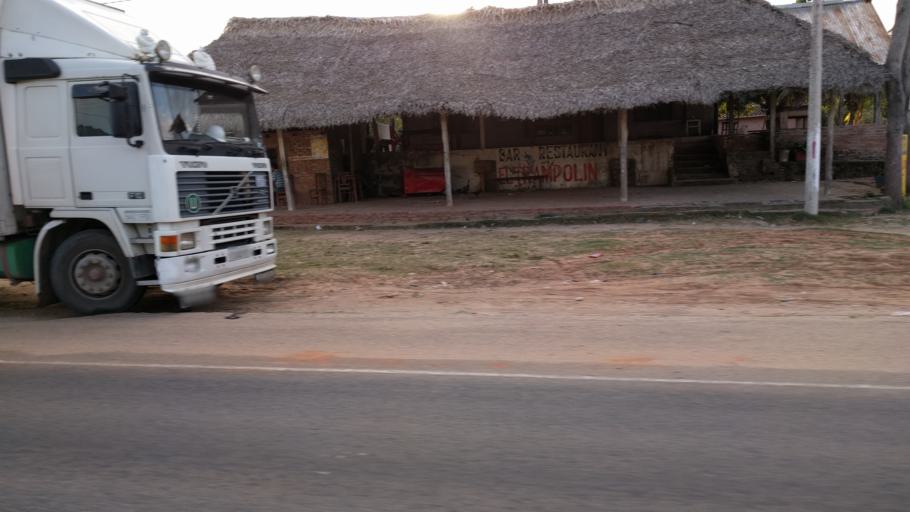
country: BO
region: Santa Cruz
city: Buena Vista
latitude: -17.4152
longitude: -63.6176
